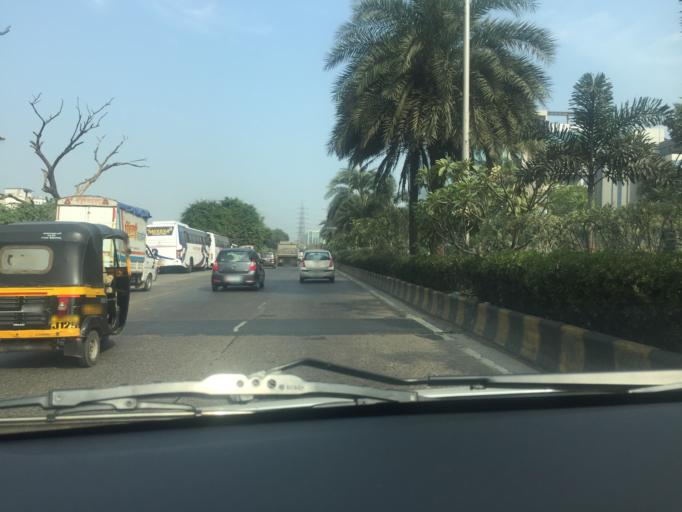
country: IN
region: Maharashtra
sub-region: Thane
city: Airoli
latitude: 19.1610
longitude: 72.9999
